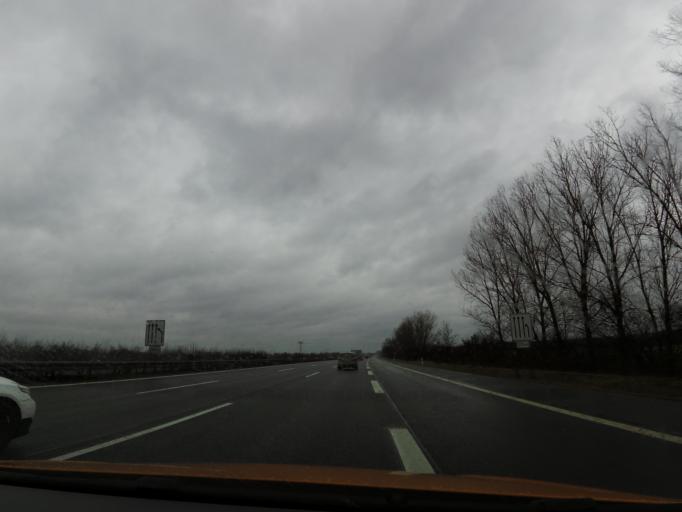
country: DE
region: Brandenburg
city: Schulzendorf
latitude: 52.3341
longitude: 13.5541
